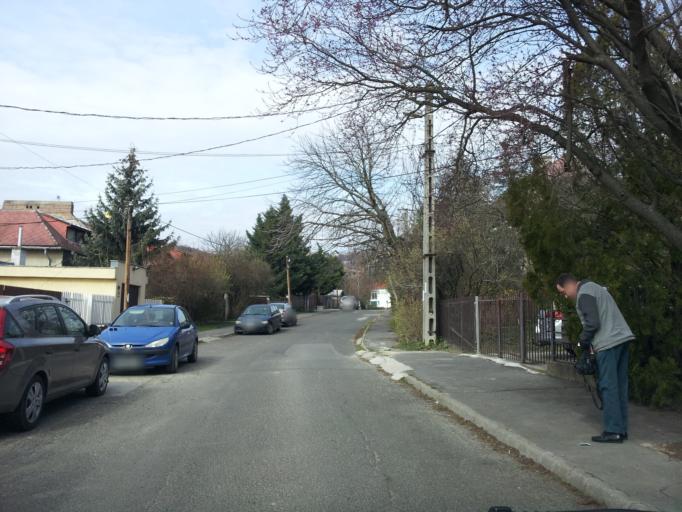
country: HU
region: Budapest
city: Budapest XII. keruelet
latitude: 47.4806
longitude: 18.9956
